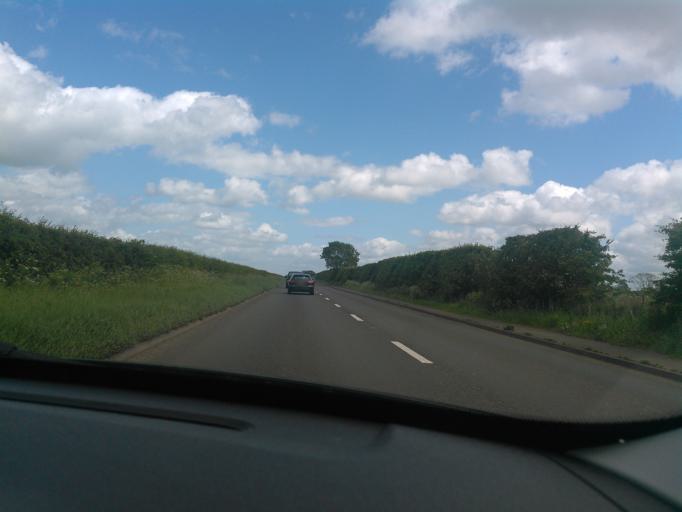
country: GB
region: England
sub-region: Shropshire
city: Stoke upon Tern
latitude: 52.8876
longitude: -2.5395
